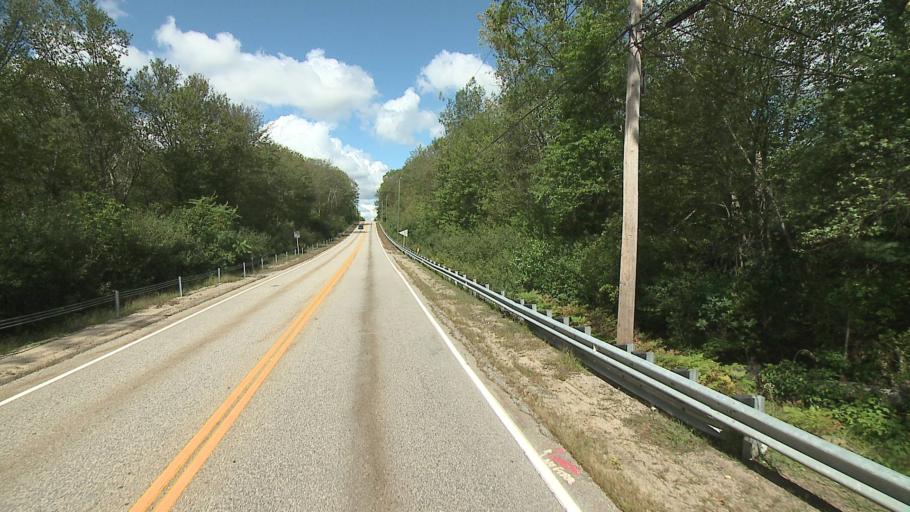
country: US
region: Connecticut
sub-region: Windham County
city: South Woodstock
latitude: 41.8635
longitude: -72.0450
